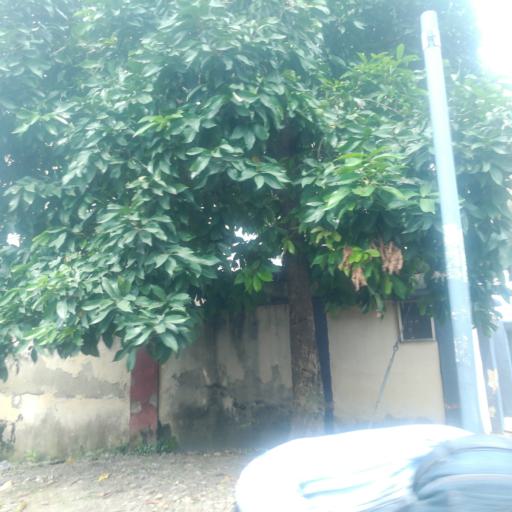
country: NG
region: Lagos
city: Ojota
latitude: 6.5753
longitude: 3.3945
